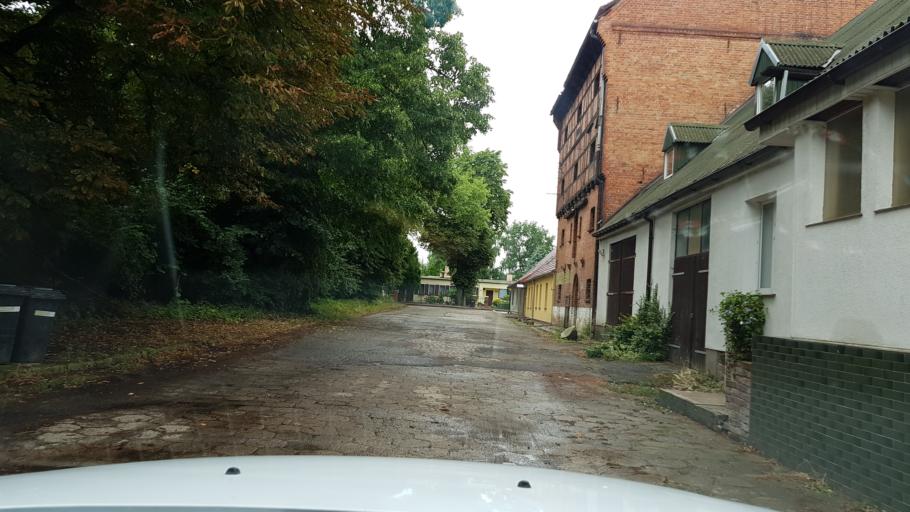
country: PL
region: West Pomeranian Voivodeship
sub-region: Powiat pyrzycki
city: Przelewice
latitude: 53.1108
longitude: 15.1063
